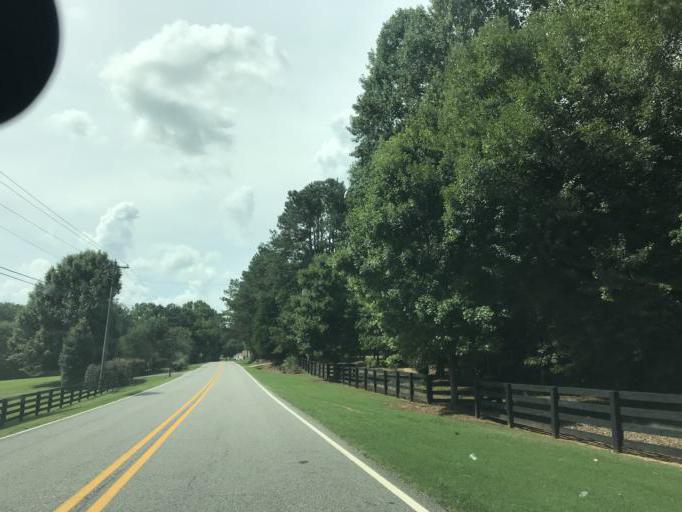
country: US
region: Georgia
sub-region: Forsyth County
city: Cumming
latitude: 34.2237
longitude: -84.2414
